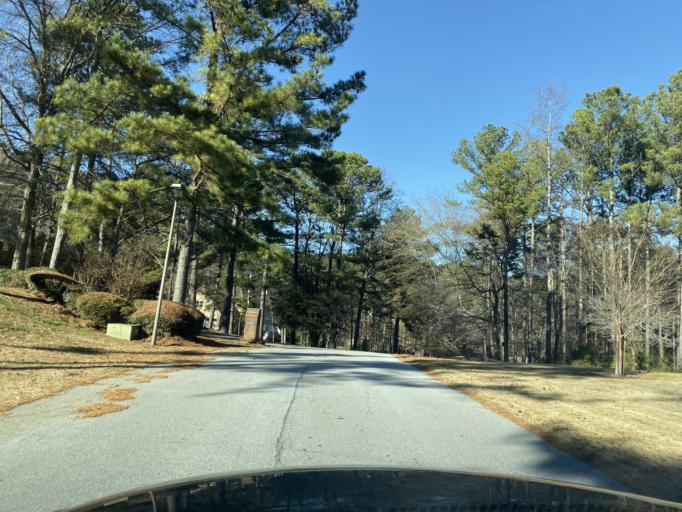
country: US
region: Georgia
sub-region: DeKalb County
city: Pine Mountain
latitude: 33.6808
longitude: -84.1659
